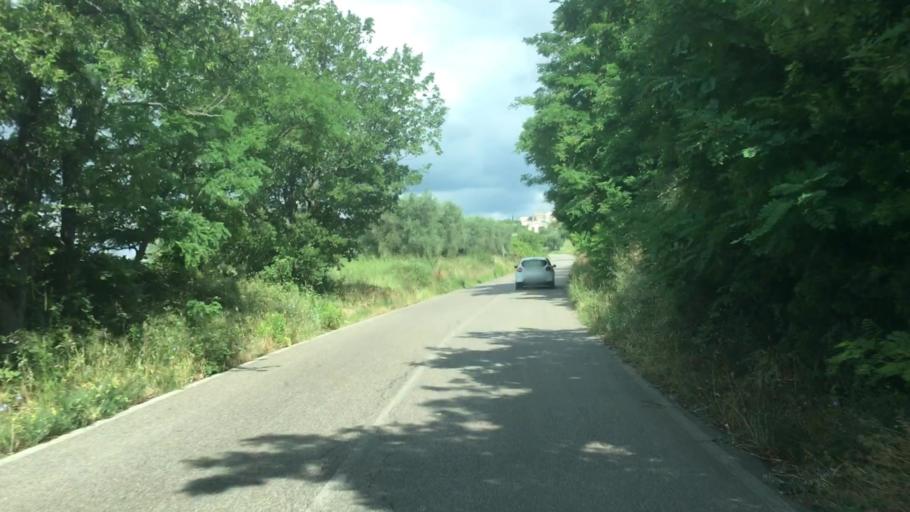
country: IT
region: Basilicate
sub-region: Provincia di Matera
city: San Mauro Forte
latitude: 40.4802
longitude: 16.2632
